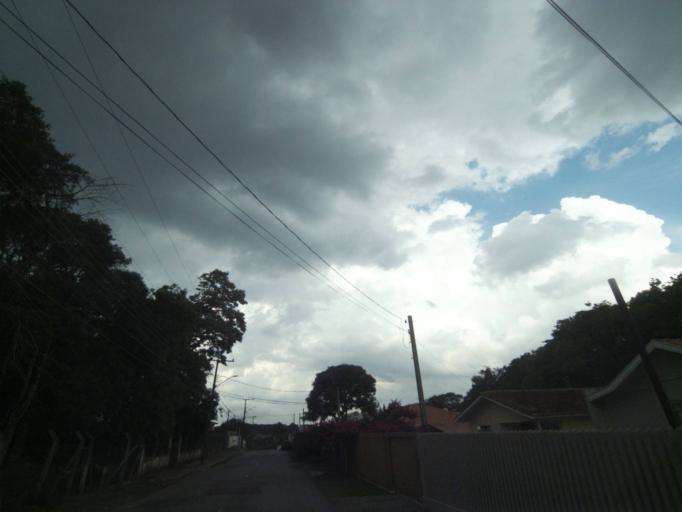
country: BR
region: Parana
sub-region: Curitiba
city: Curitiba
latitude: -25.4519
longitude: -49.3473
